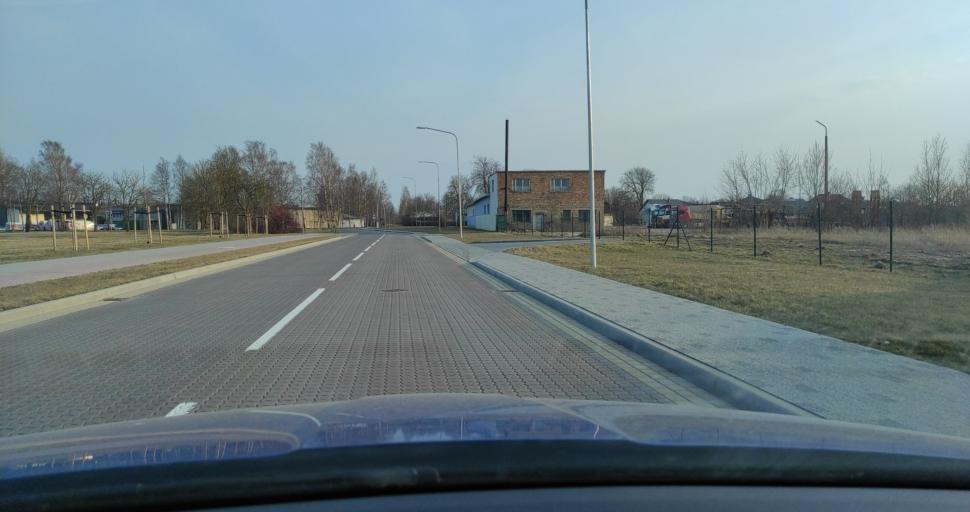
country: LV
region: Ventspils
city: Ventspils
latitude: 57.3843
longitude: 21.5820
